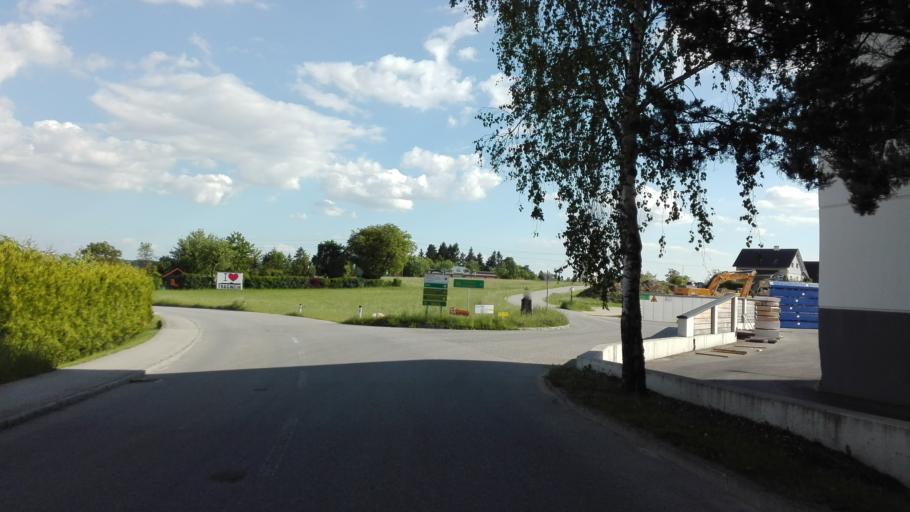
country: AT
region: Upper Austria
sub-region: Politischer Bezirk Perg
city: Perg
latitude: 48.3266
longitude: 14.6228
